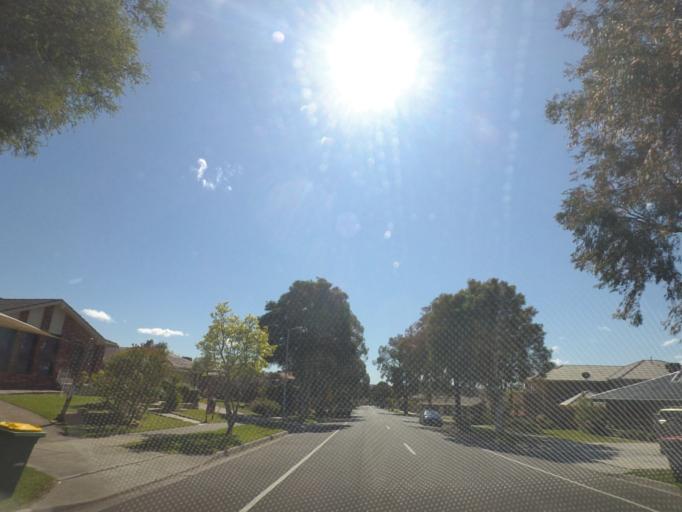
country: AU
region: Victoria
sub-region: Knox
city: Wantirna South
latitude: -37.8841
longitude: 145.2243
